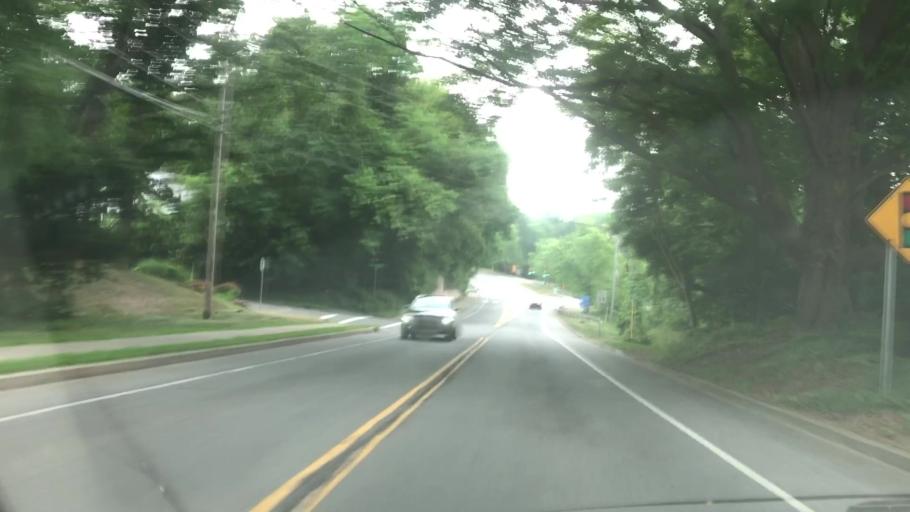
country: US
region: New York
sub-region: Monroe County
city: East Rochester
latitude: 43.1228
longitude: -77.4759
